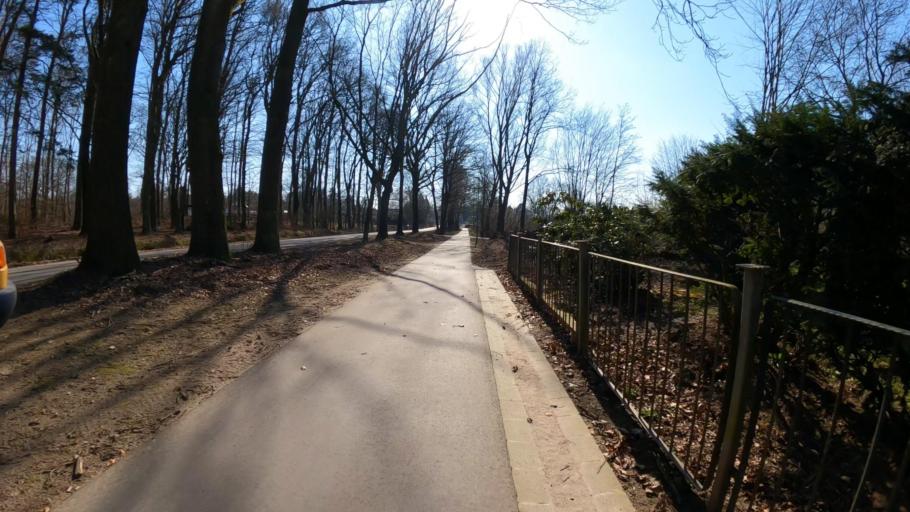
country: DE
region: Lower Saxony
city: Bendestorf
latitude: 53.3536
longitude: 9.9227
